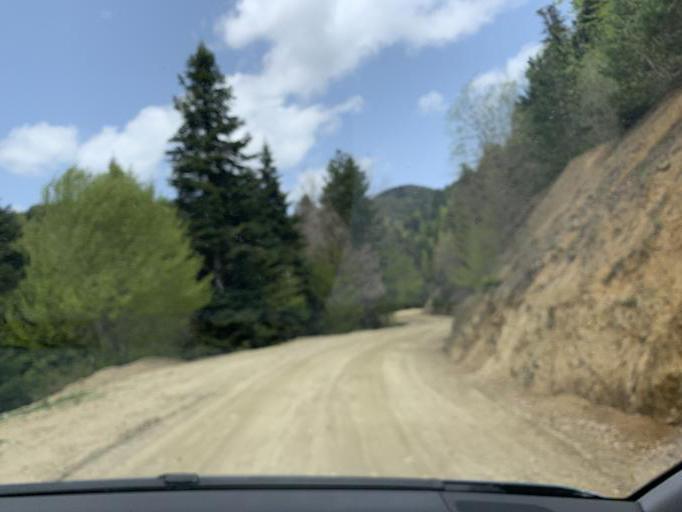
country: TR
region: Bolu
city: Bolu
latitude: 40.8361
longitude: 31.6706
